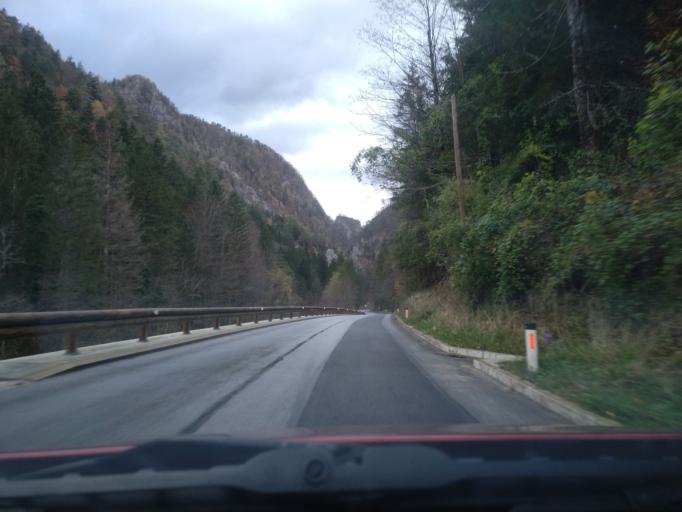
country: SI
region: Luce
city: Luce
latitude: 46.3764
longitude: 14.7324
